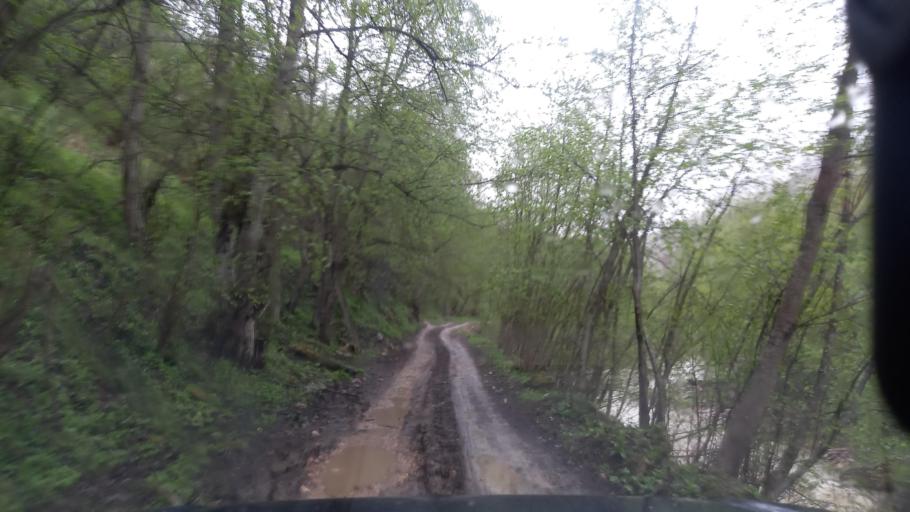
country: RU
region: Kabardino-Balkariya
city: Bylym
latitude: 43.5996
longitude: 42.9225
